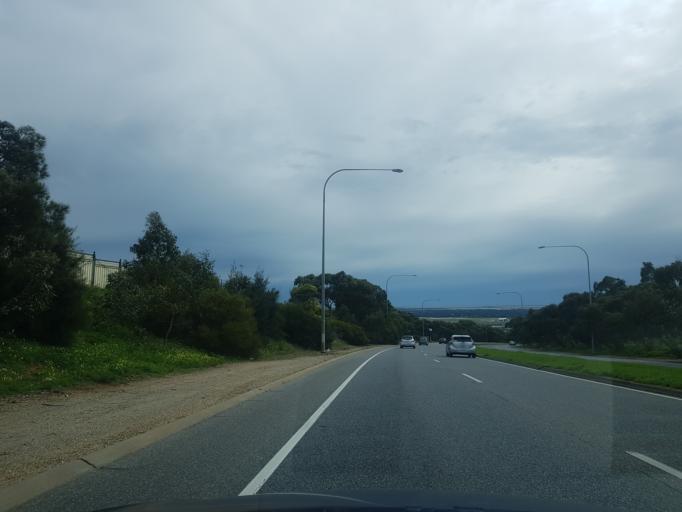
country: AU
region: South Australia
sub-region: Tea Tree Gully
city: Modbury
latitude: -34.8084
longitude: 138.6707
